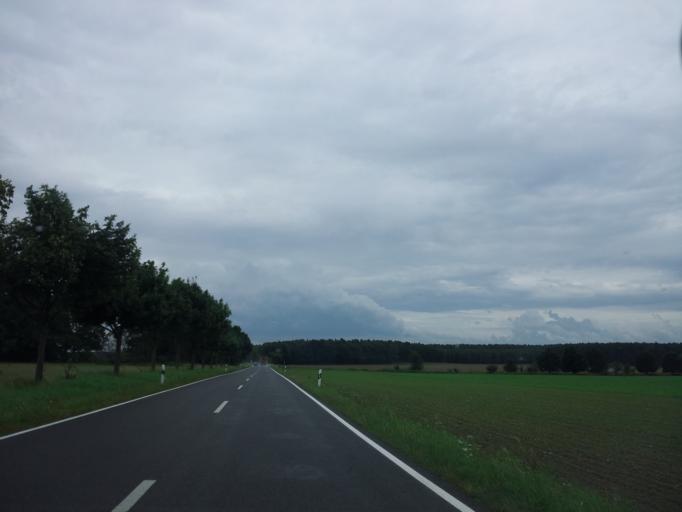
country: DE
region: Brandenburg
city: Wiesenburg
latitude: 52.1629
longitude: 12.4851
